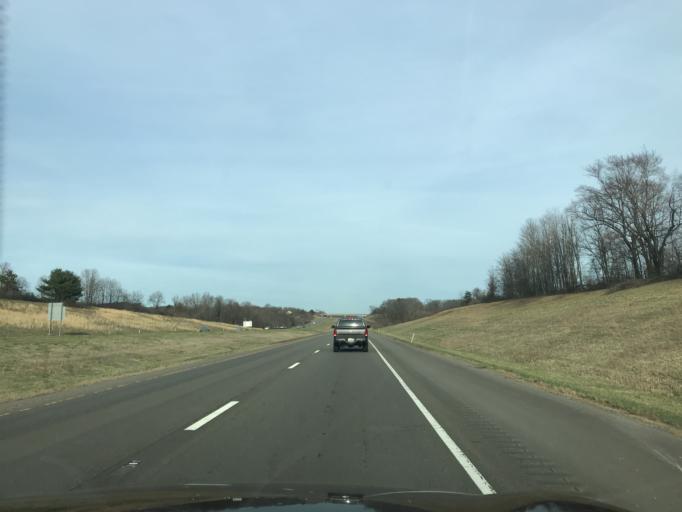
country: US
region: Pennsylvania
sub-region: Lycoming County
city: Montoursville
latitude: 41.2527
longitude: -76.8740
